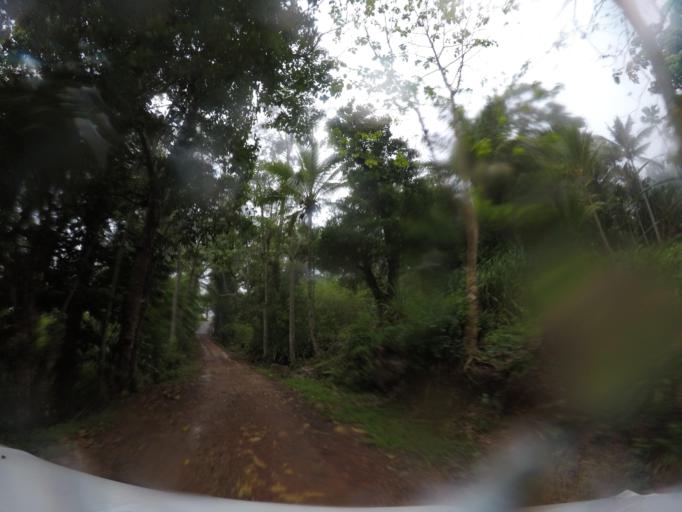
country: TL
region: Baucau
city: Venilale
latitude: -8.6328
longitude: 126.4248
